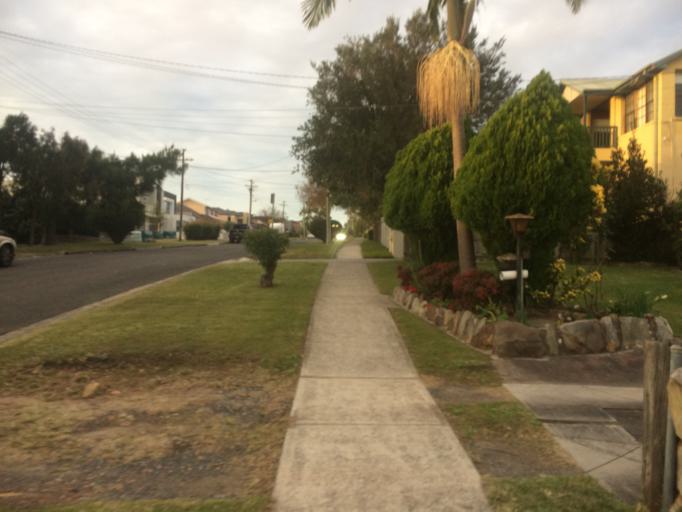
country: AU
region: New South Wales
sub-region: Canada Bay
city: Rhodes
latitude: -33.8291
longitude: 151.1041
